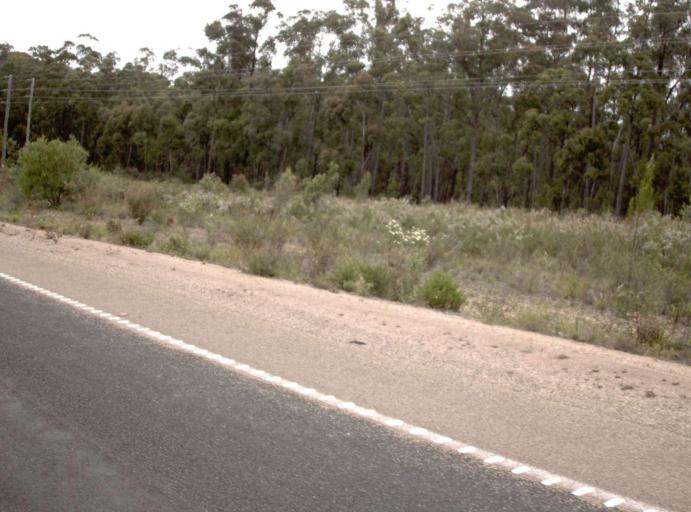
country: AU
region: Victoria
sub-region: East Gippsland
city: Lakes Entrance
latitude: -37.7007
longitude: 148.0502
